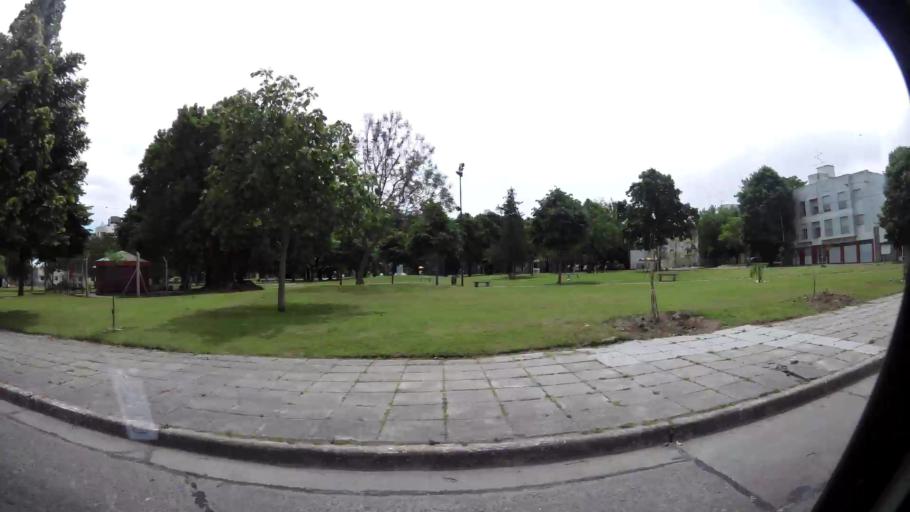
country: AR
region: Buenos Aires
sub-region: Partido de La Plata
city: La Plata
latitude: -34.9374
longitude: -57.9463
